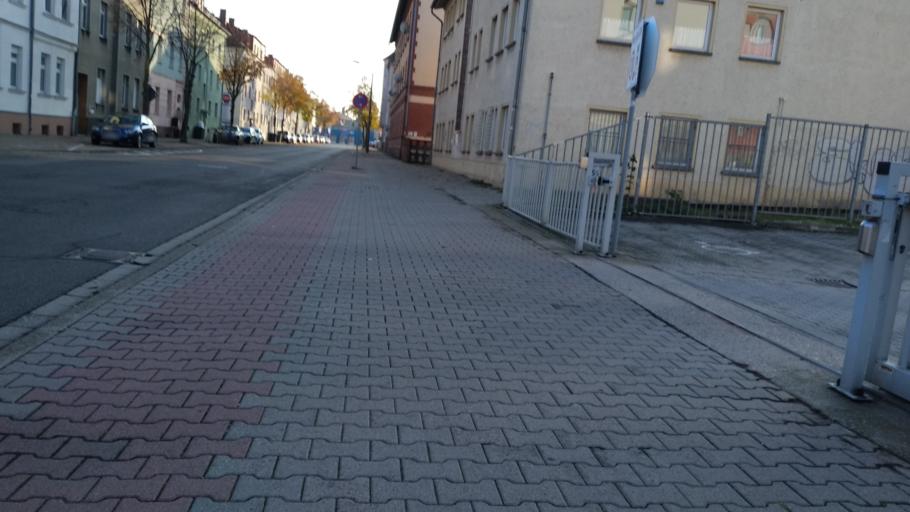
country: DE
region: Saxony
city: Bitterfeld-Wolfen
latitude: 51.6208
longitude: 12.3179
